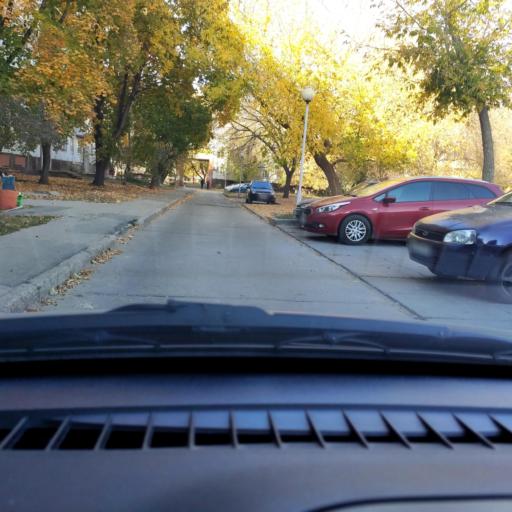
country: RU
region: Samara
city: Tol'yatti
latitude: 53.5339
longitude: 49.2641
